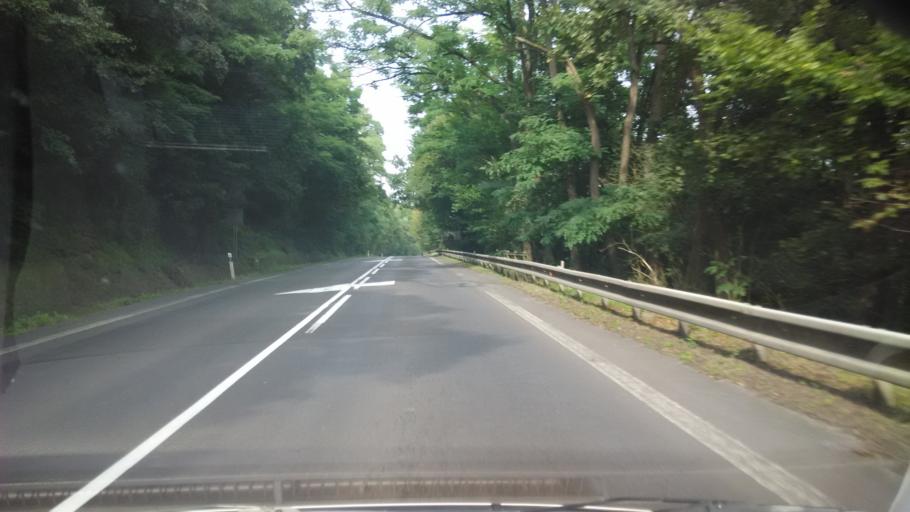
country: SK
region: Banskobystricky
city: Krupina
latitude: 48.2670
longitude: 18.9912
